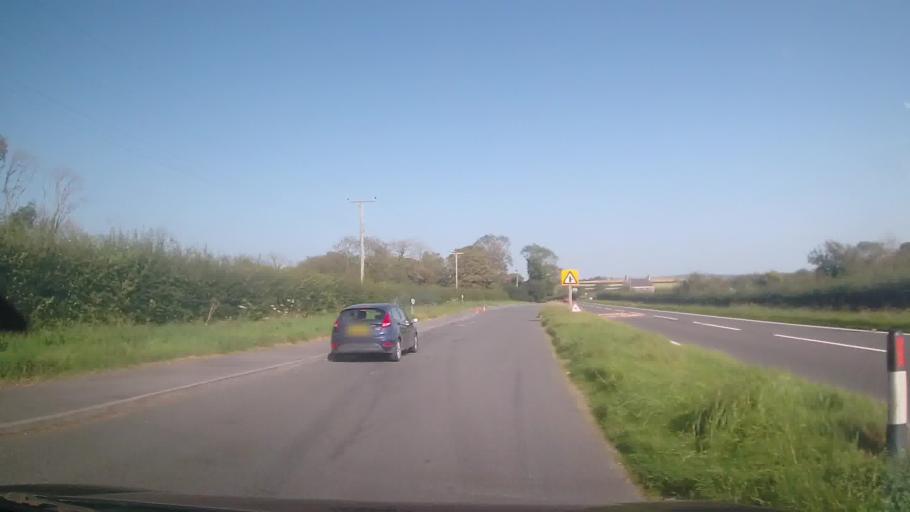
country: GB
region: Wales
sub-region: County of Ceredigion
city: Aberporth
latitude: 52.1080
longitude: -4.5832
